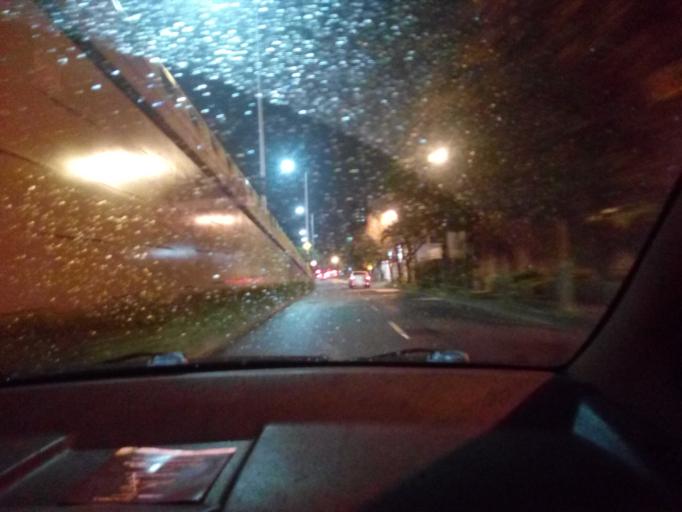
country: CO
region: Antioquia
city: Envigado
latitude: 6.1745
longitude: -75.5916
